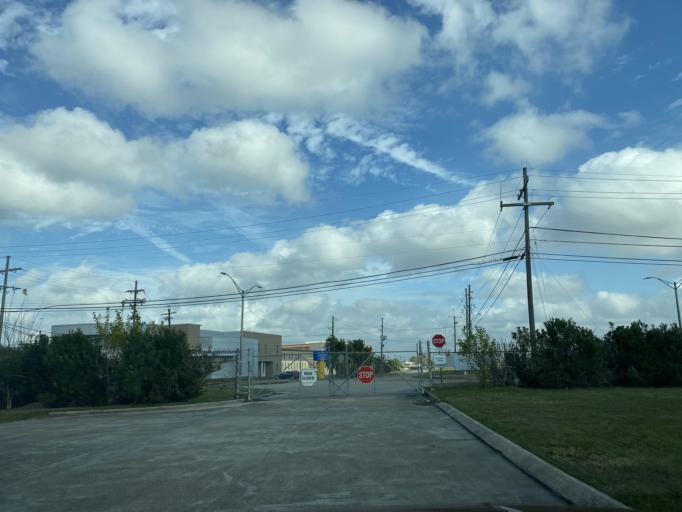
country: US
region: Louisiana
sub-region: Orleans Parish
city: New Orleans
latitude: 30.0293
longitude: -90.0466
